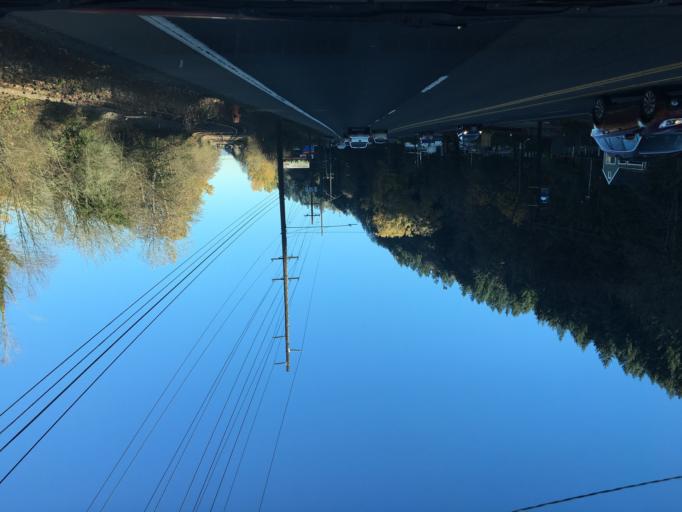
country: US
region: Oregon
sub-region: Washington County
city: West Haven
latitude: 45.5680
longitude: -122.7520
